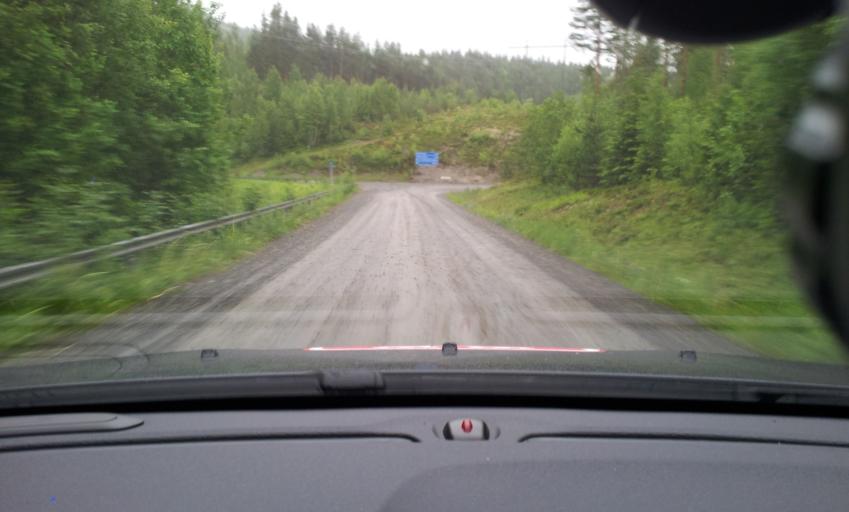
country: SE
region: Jaemtland
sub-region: Ragunda Kommun
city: Hammarstrand
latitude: 63.1322
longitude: 16.0726
